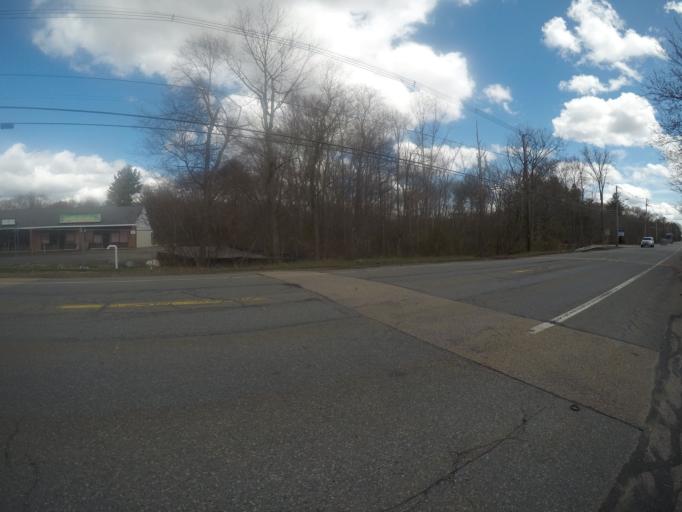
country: US
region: Massachusetts
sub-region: Bristol County
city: Easton
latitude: 42.0364
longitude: -71.0743
